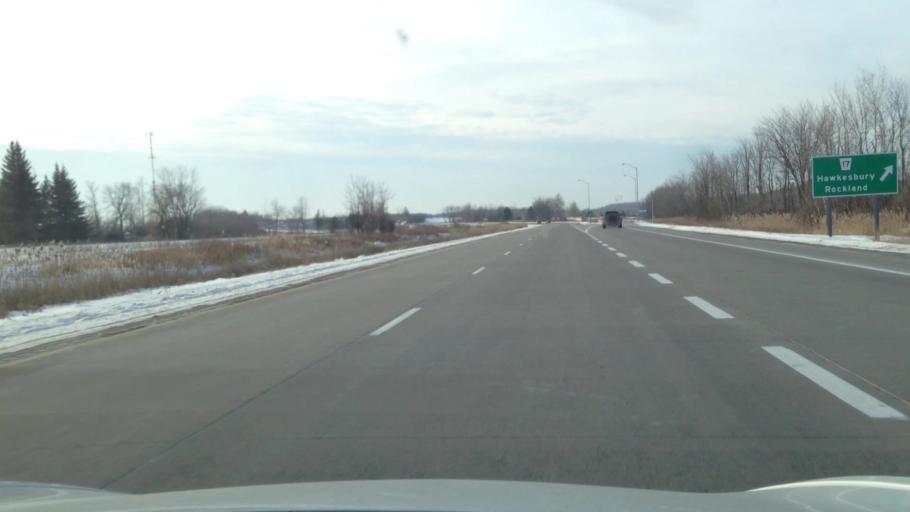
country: CA
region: Ontario
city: Hawkesbury
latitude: 45.5643
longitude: -74.4943
